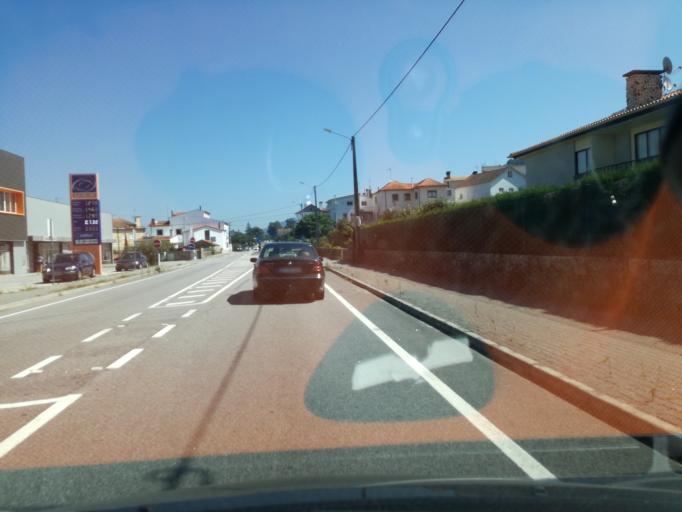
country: ES
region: Galicia
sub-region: Provincia de Pontevedra
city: O Rosal
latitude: 41.9084
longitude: -8.7935
